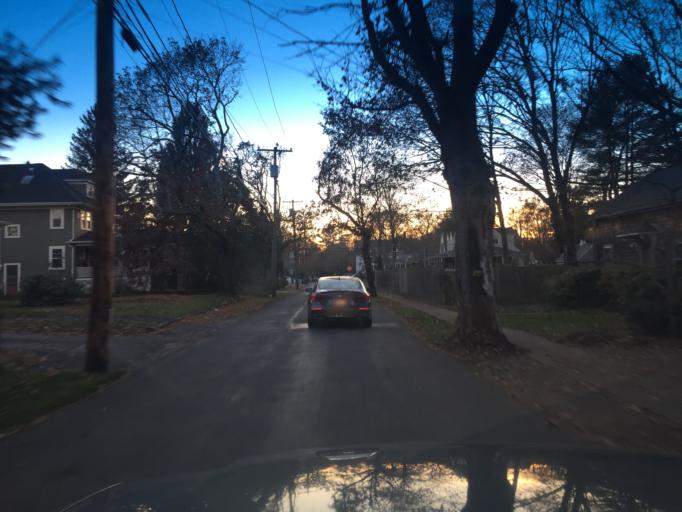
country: US
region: Massachusetts
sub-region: Norfolk County
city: Medfield
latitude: 42.1848
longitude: -71.3015
